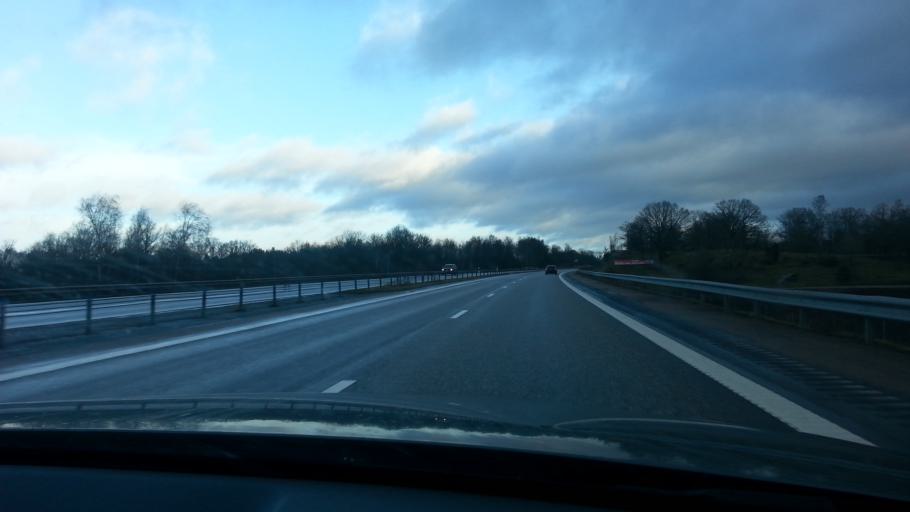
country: SE
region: OEstergoetland
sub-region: Odeshogs Kommun
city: OEdeshoeg
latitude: 58.1740
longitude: 14.5887
